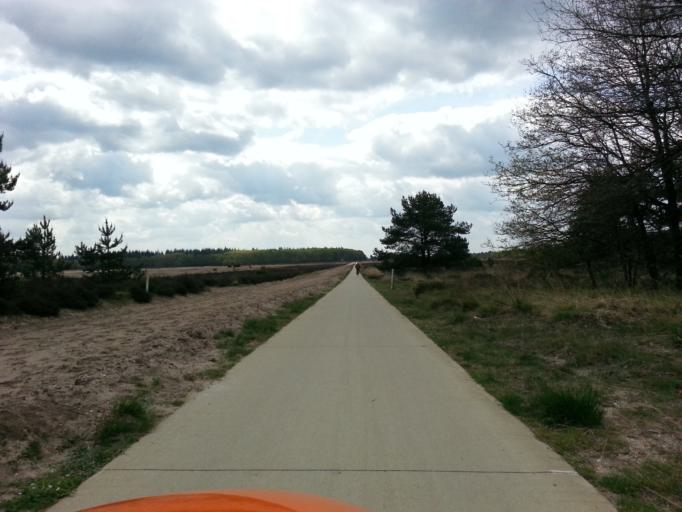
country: NL
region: Gelderland
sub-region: Gemeente Ede
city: Ede
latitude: 52.0589
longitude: 5.6985
